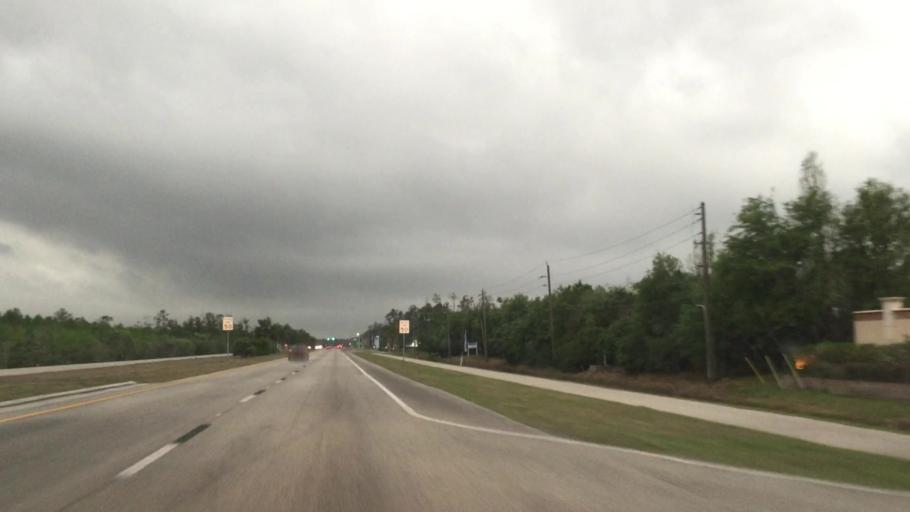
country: US
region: Florida
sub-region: Lee County
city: Fort Myers
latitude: 26.5760
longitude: -81.8258
